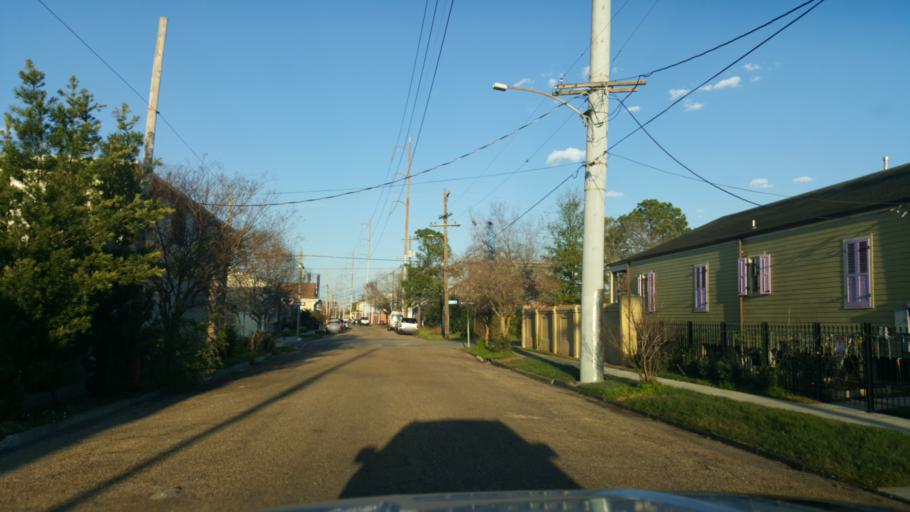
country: US
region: Louisiana
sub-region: Jefferson Parish
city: Harvey
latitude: 29.9226
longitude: -90.0759
